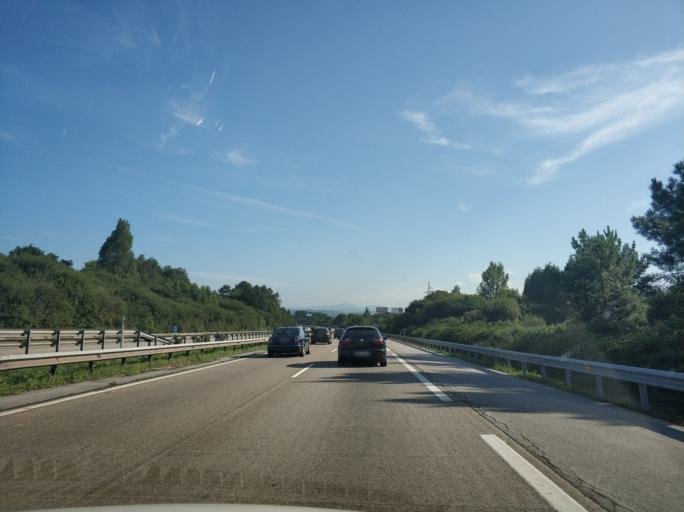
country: ES
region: Asturias
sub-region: Province of Asturias
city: Lugones
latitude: 43.4296
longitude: -5.8022
